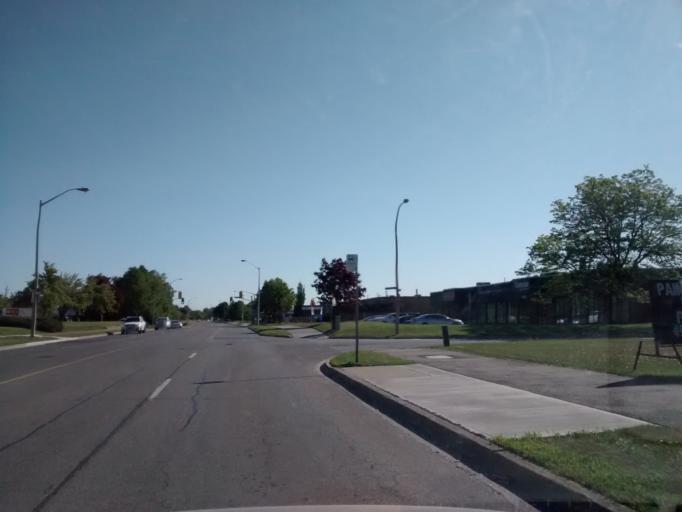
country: CA
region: Ontario
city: Burlington
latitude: 43.3669
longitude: -79.8005
